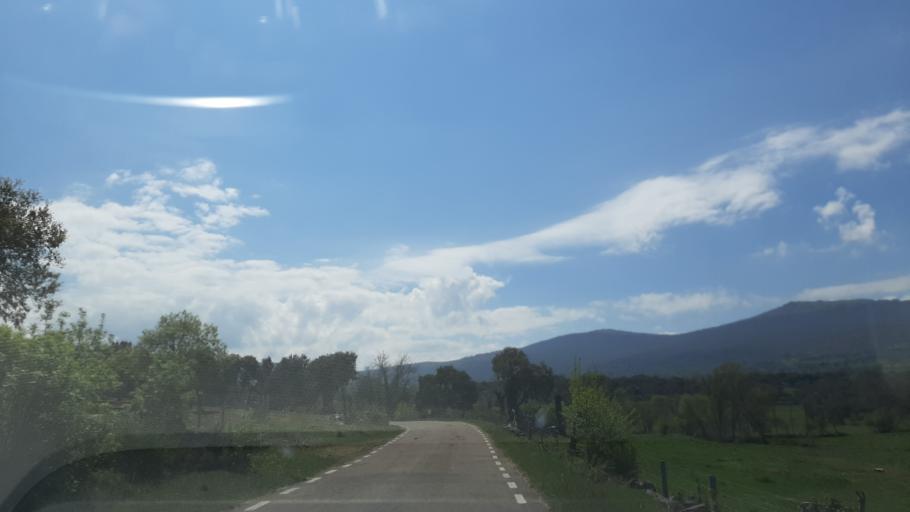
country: ES
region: Castille and Leon
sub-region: Provincia de Salamanca
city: Tejeda y Segoyuela
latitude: 40.6242
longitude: -6.0219
